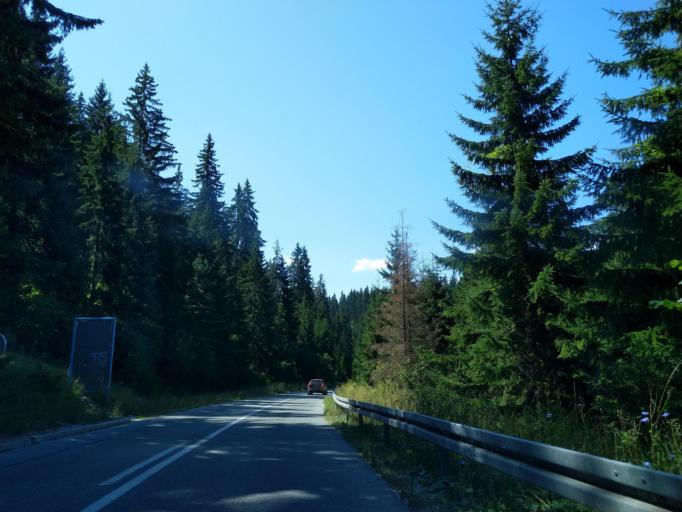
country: RS
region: Central Serbia
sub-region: Zlatiborski Okrug
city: Nova Varos
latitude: 43.3995
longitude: 19.8446
